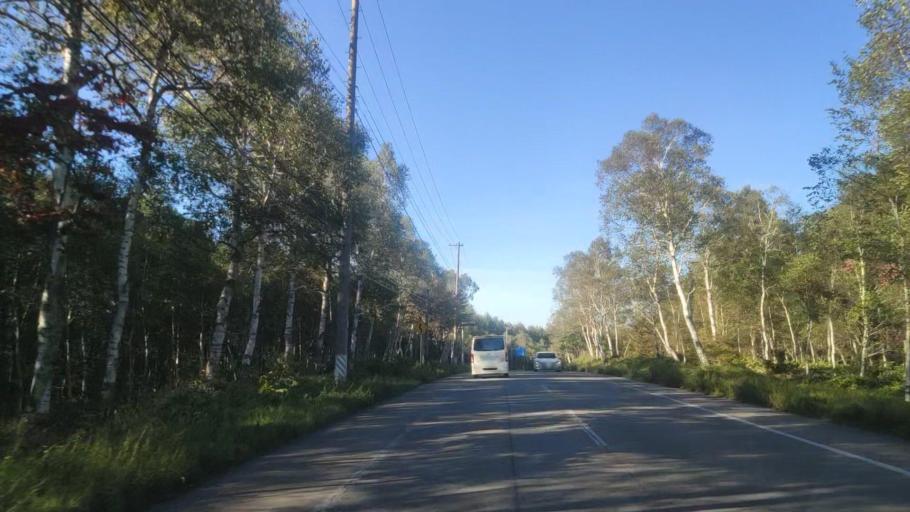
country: JP
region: Nagano
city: Kamimaruko
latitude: 36.1666
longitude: 138.2803
